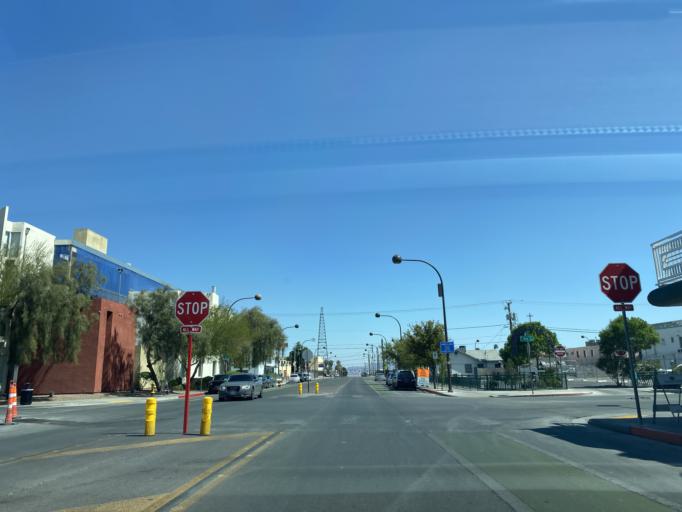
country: US
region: Nevada
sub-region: Clark County
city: Las Vegas
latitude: 36.1691
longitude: -115.1368
